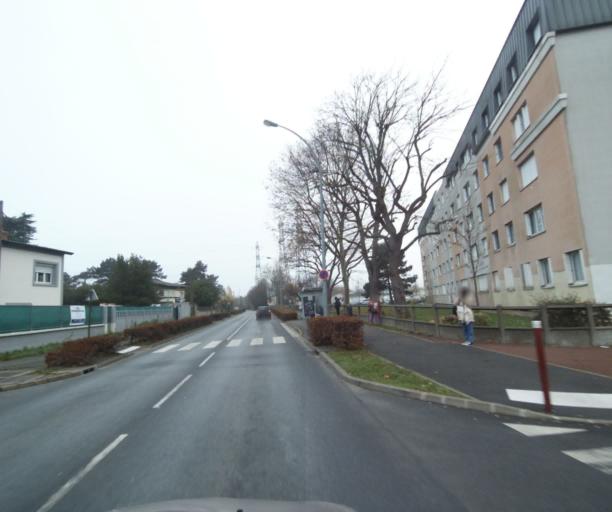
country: FR
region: Ile-de-France
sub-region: Departement de Seine-Saint-Denis
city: Gagny
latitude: 48.8719
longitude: 2.5334
